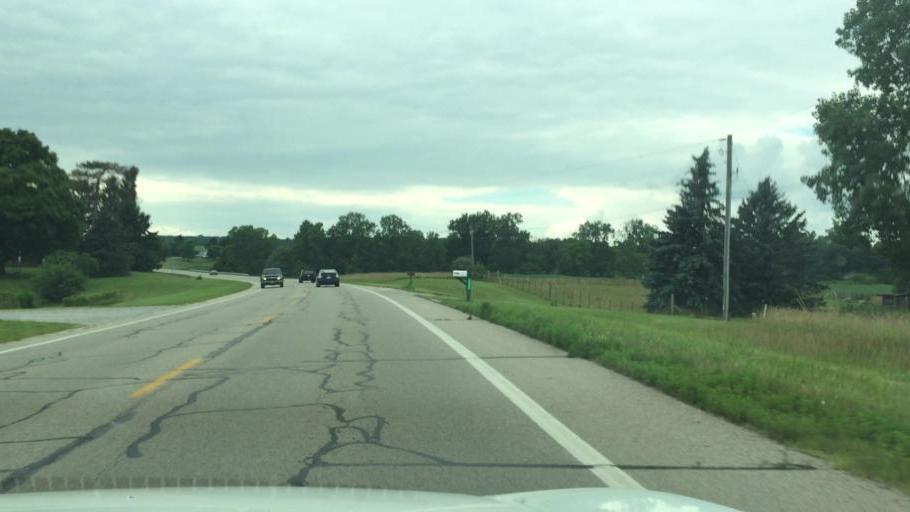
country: US
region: Ohio
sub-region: Champaign County
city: Mechanicsburg
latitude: 40.0778
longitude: -83.5766
